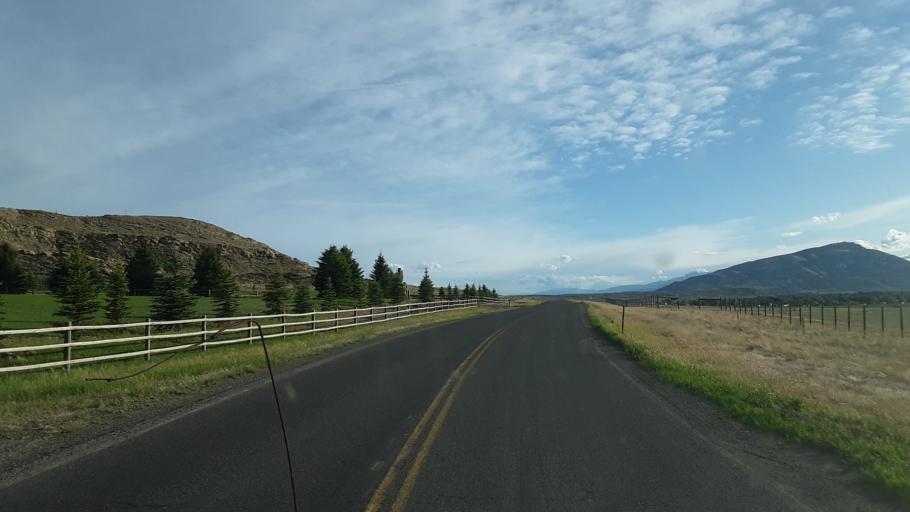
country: US
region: Wyoming
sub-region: Park County
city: Cody
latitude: 44.5261
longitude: -109.0093
